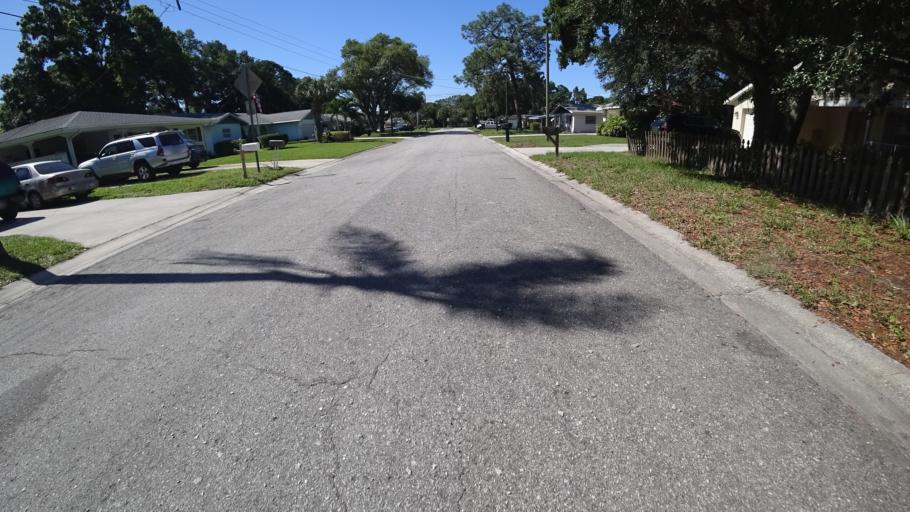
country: US
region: Florida
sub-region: Manatee County
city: West Bradenton
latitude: 27.4898
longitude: -82.5989
